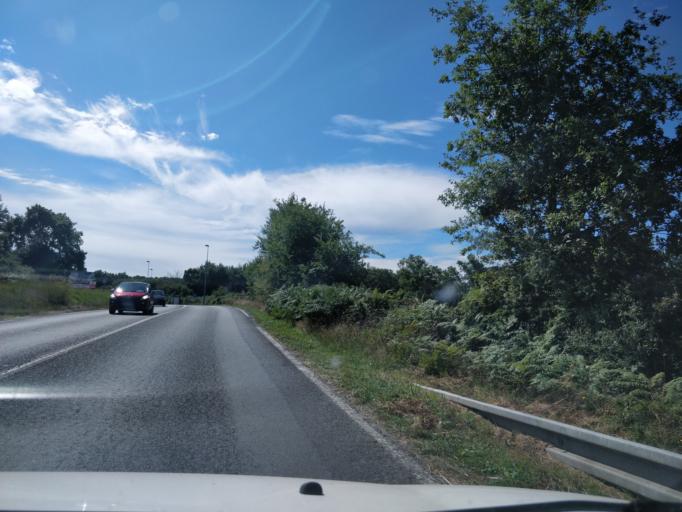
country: FR
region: Brittany
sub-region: Departement du Morbihan
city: Saint-Philibert
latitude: 47.5997
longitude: -2.9920
